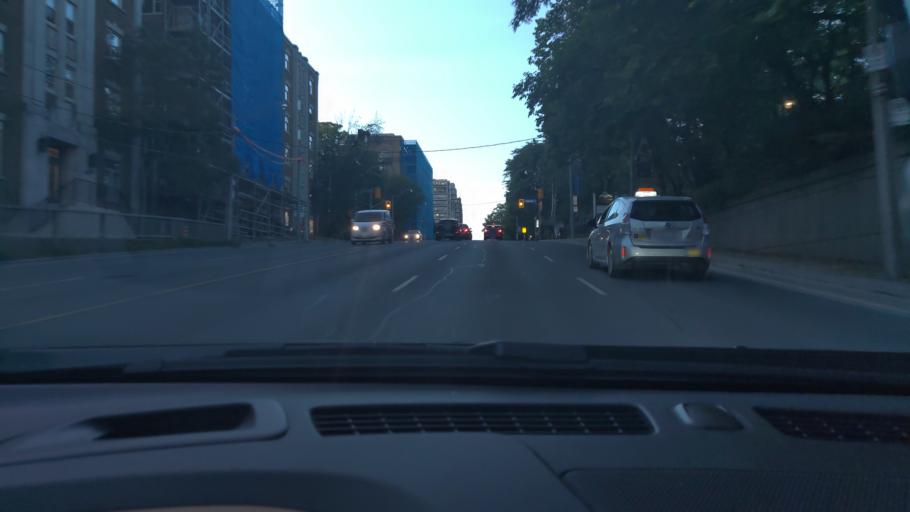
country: CA
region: Ontario
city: Toronto
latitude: 43.6816
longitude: -79.3994
